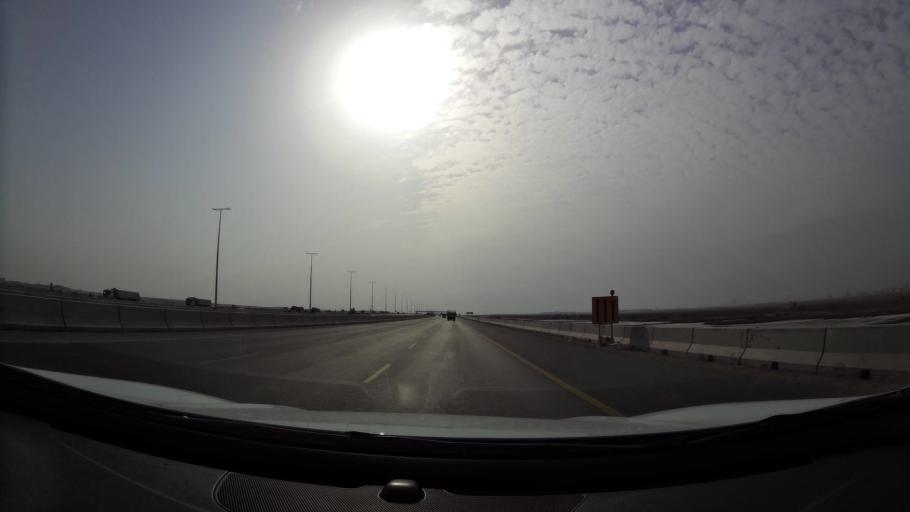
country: AE
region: Abu Dhabi
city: Abu Dhabi
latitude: 24.2834
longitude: 54.5384
